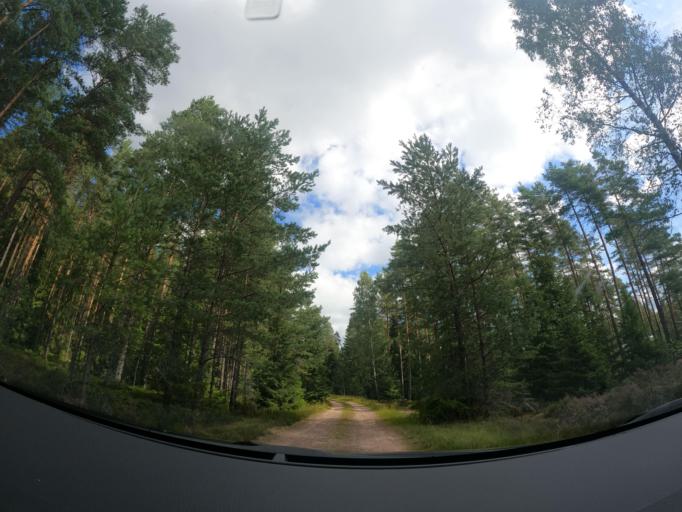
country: SE
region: Joenkoeping
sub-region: Gislaveds Kommun
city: Gislaved
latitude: 57.4261
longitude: 13.6096
